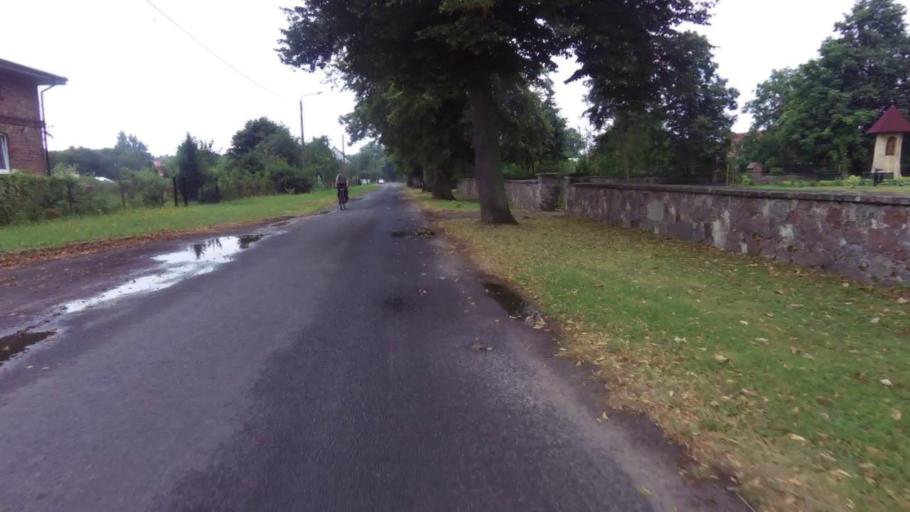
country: PL
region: West Pomeranian Voivodeship
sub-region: Powiat choszczenski
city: Choszczno
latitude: 53.2281
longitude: 15.3810
